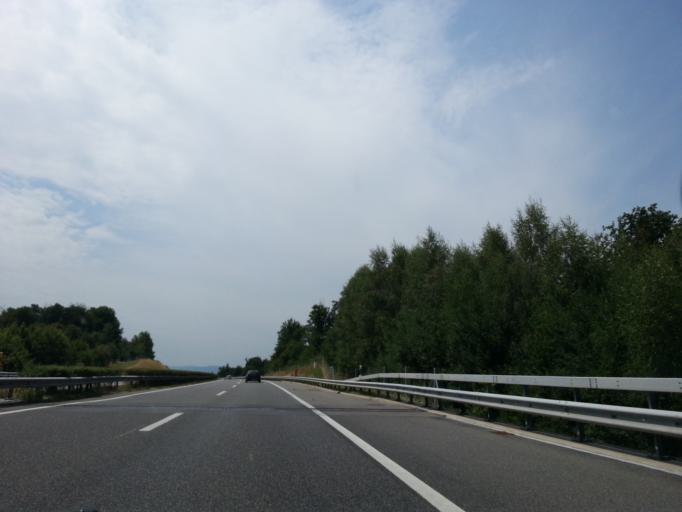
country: CH
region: Vaud
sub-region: Jura-Nord vaudois District
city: Yvonand
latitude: 46.7758
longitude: 6.7220
